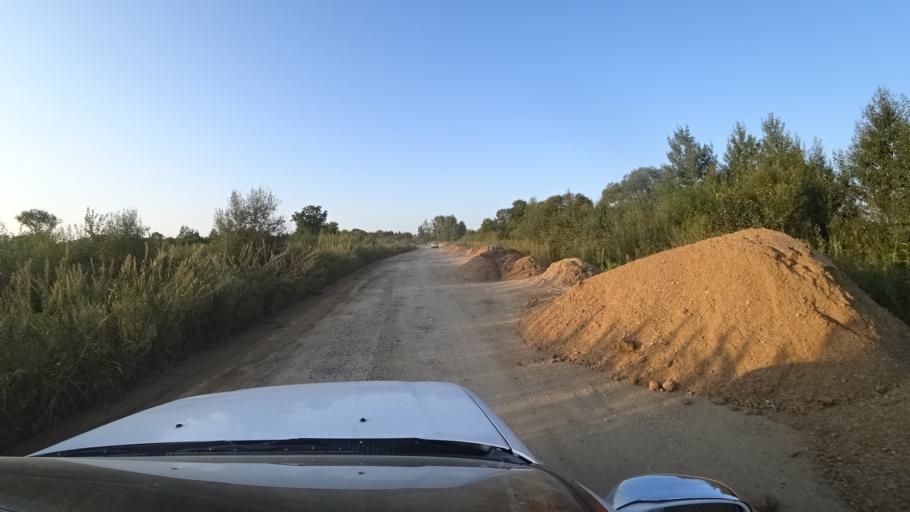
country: RU
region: Primorskiy
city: Dal'nerechensk
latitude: 45.9400
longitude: 133.7607
